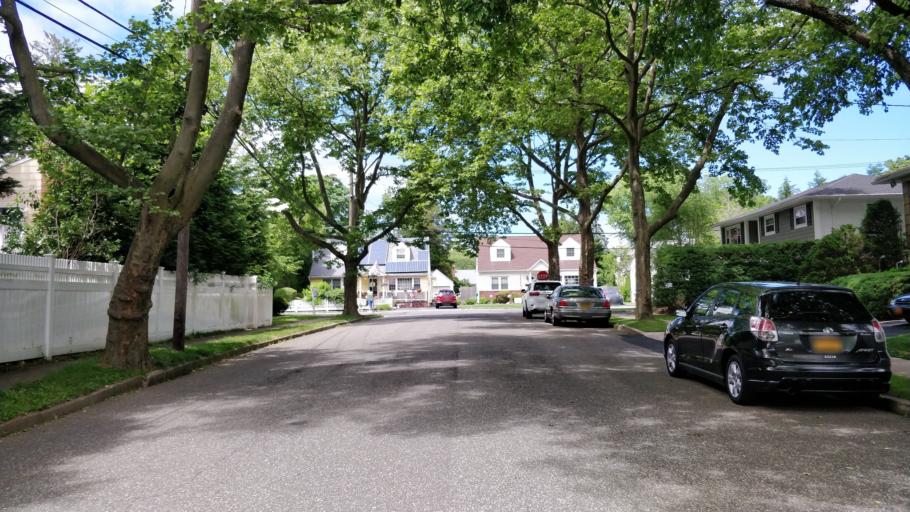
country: US
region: New York
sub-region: Suffolk County
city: South Huntington
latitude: 40.8071
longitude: -73.4039
